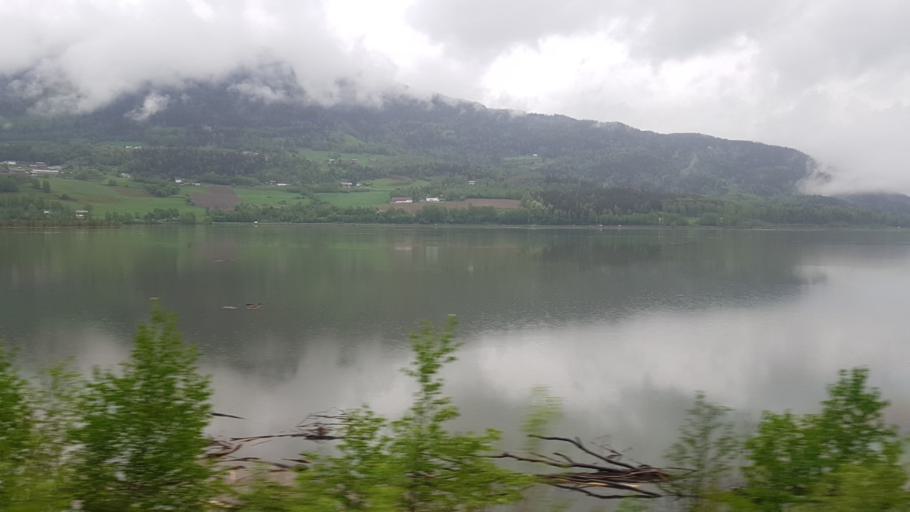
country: NO
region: Oppland
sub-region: Oyer
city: Tretten
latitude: 61.3901
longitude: 10.2541
